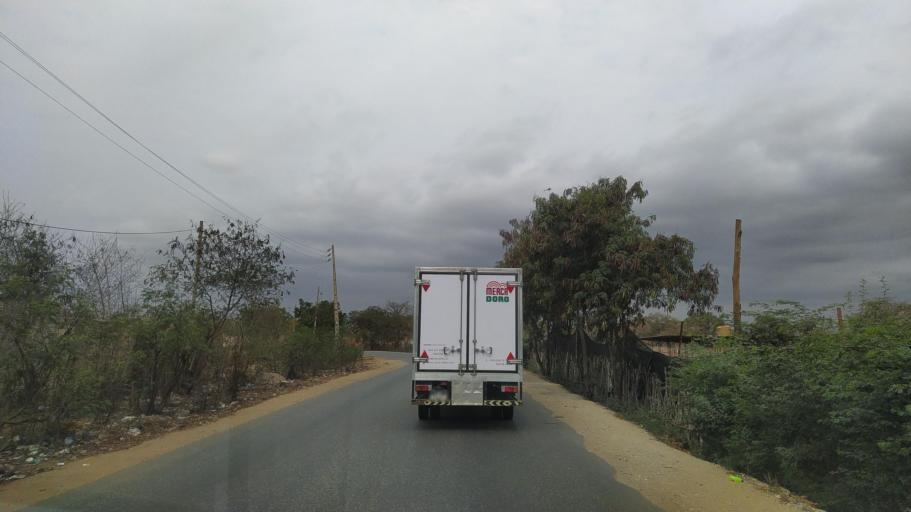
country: AO
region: Luanda
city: Luanda
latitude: -8.8581
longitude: 13.2839
